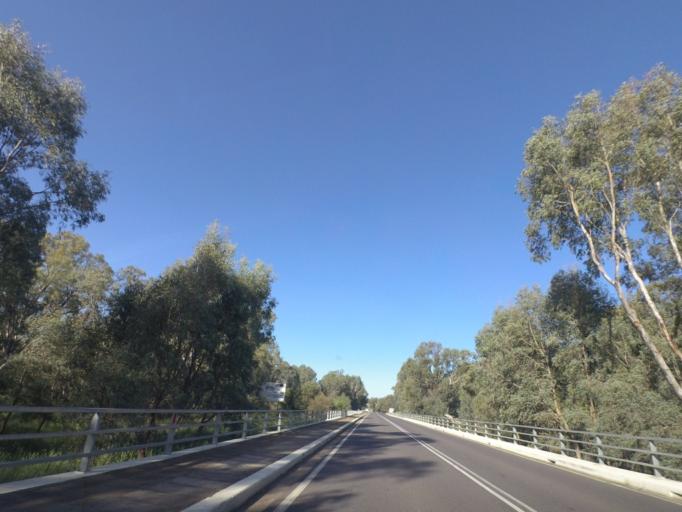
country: AU
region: New South Wales
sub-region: Wagga Wagga
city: Forest Hill
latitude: -35.2801
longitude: 147.7315
